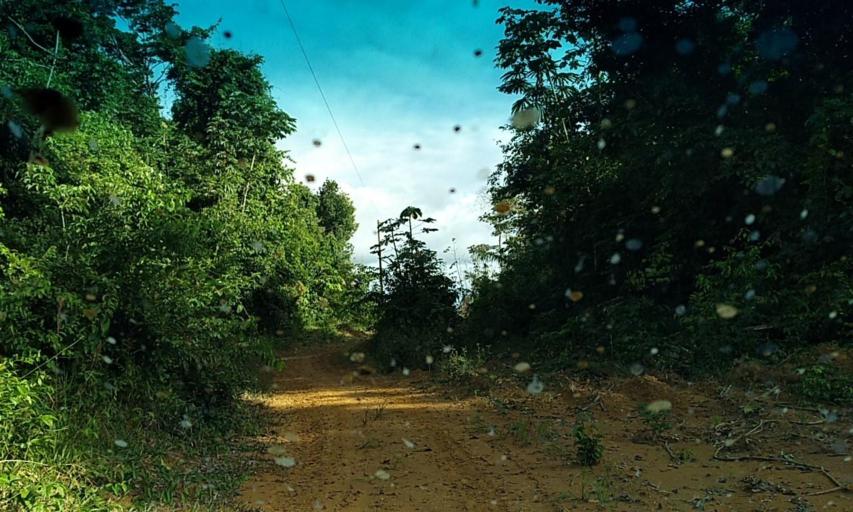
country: BR
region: Para
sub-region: Senador Jose Porfirio
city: Senador Jose Porfirio
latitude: -2.9952
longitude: -51.7430
